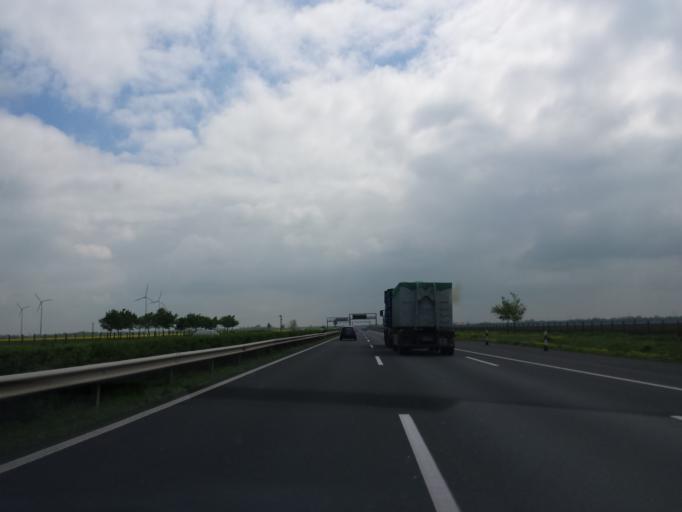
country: HU
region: Gyor-Moson-Sopron
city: Mosonmagyarovar
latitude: 47.8815
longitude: 17.1962
